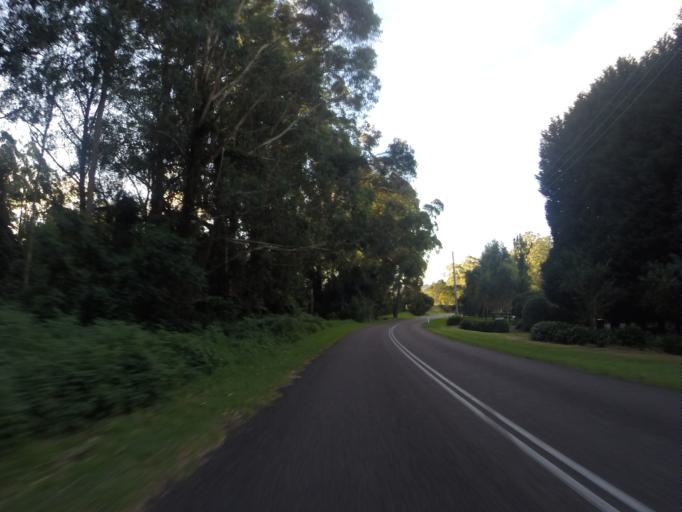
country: AU
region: New South Wales
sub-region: Shoalhaven Shire
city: Kangaroo Valley
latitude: -34.6199
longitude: 150.5298
